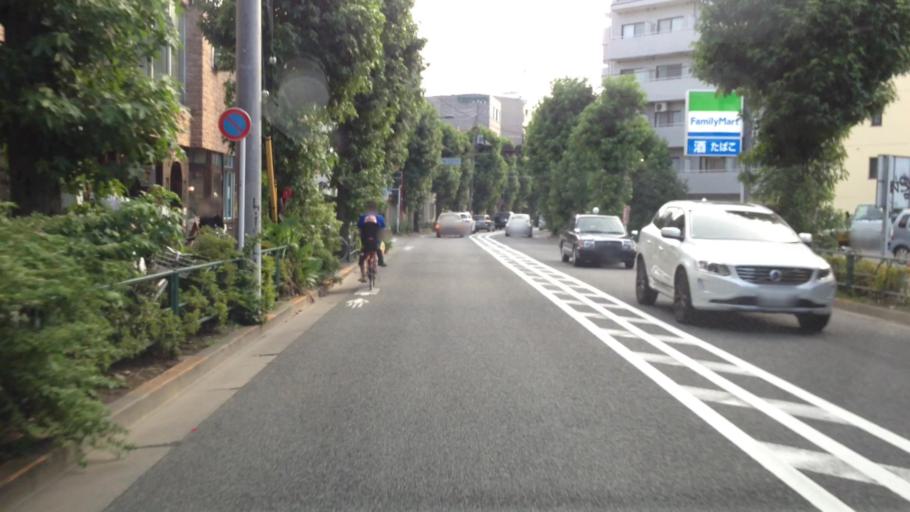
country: JP
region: Tokyo
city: Tokyo
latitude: 35.6292
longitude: 139.6813
